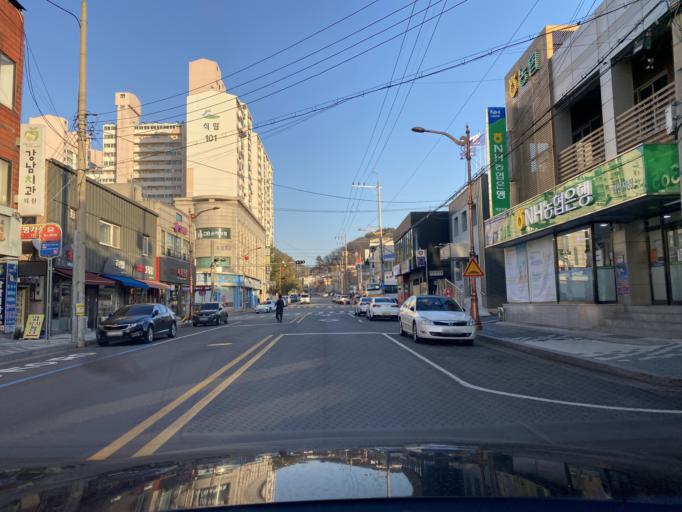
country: KR
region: Chungcheongnam-do
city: Yesan
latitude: 36.6862
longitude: 126.8315
